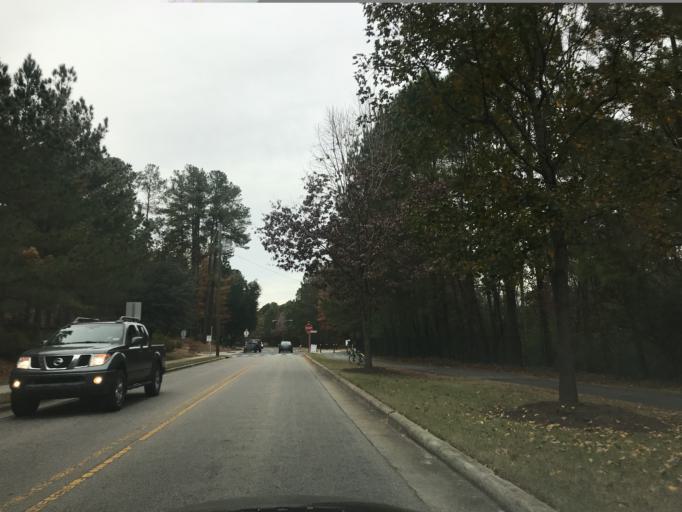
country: US
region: North Carolina
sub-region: Wake County
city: West Raleigh
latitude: 35.7861
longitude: -78.6804
